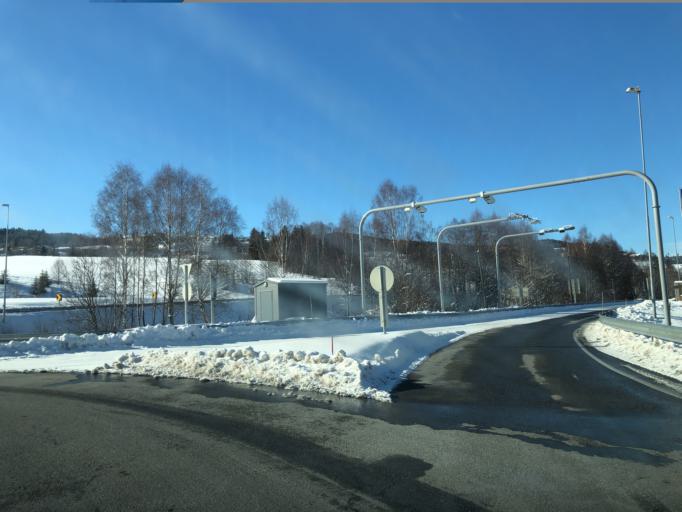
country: NO
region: Oppland
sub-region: Lunner
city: Roa
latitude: 60.3226
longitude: 10.5825
